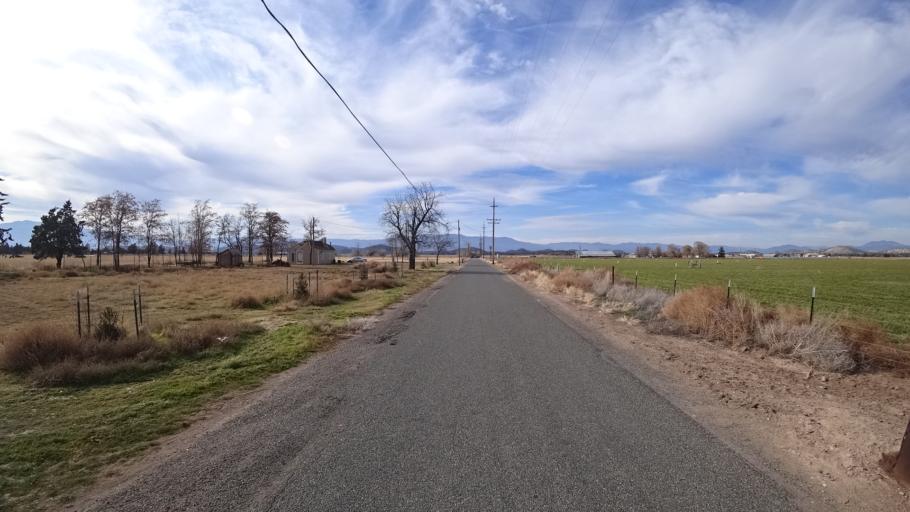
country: US
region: California
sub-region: Siskiyou County
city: Montague
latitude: 41.6165
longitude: -122.3958
